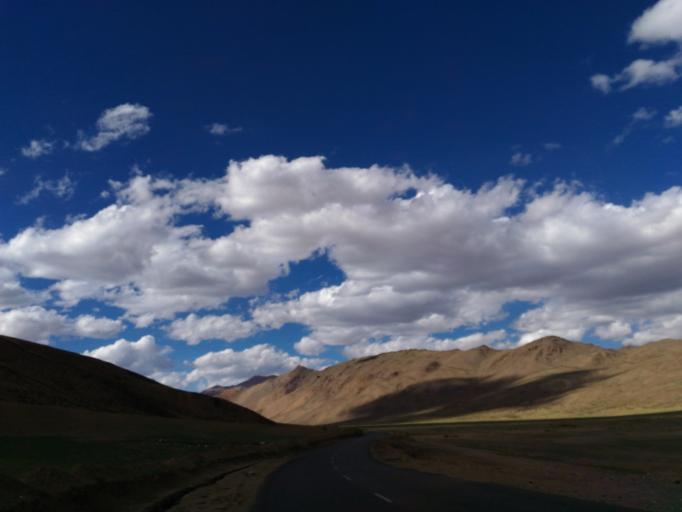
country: IN
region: Kashmir
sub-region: Ladakh
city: Leh
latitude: 33.3185
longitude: 77.9193
